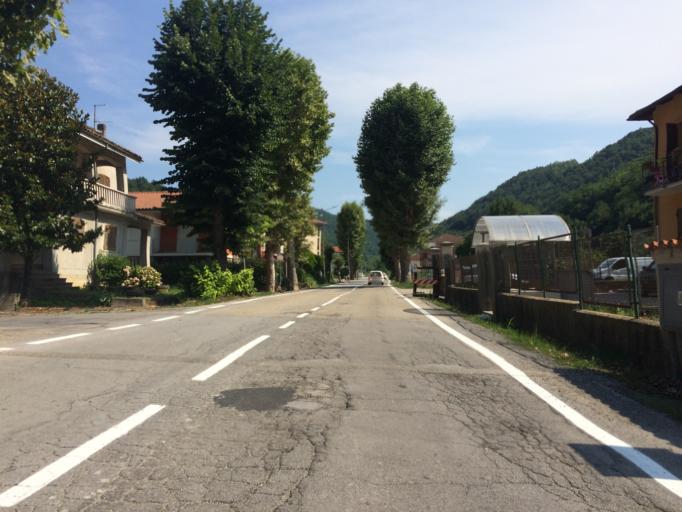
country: IT
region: Piedmont
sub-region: Provincia di Cuneo
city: Cortemilia
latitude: 44.5747
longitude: 8.1995
